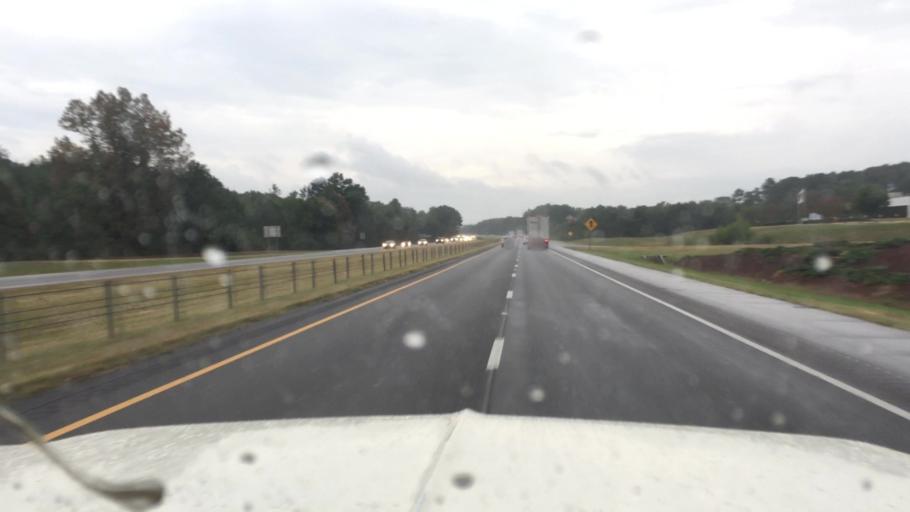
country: US
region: Alabama
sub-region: Morgan County
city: Falkville
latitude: 34.4108
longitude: -86.8984
